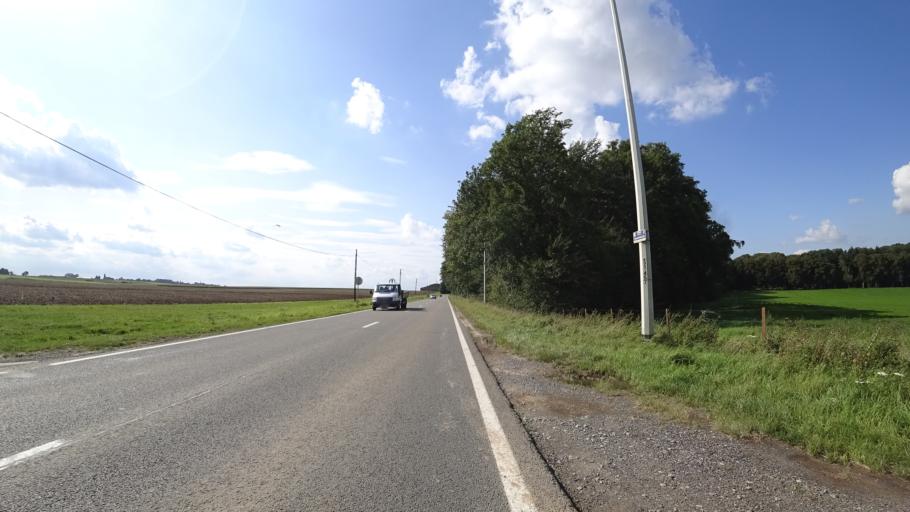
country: BE
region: Wallonia
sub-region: Province de Namur
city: Floreffe
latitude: 50.4894
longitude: 4.7465
